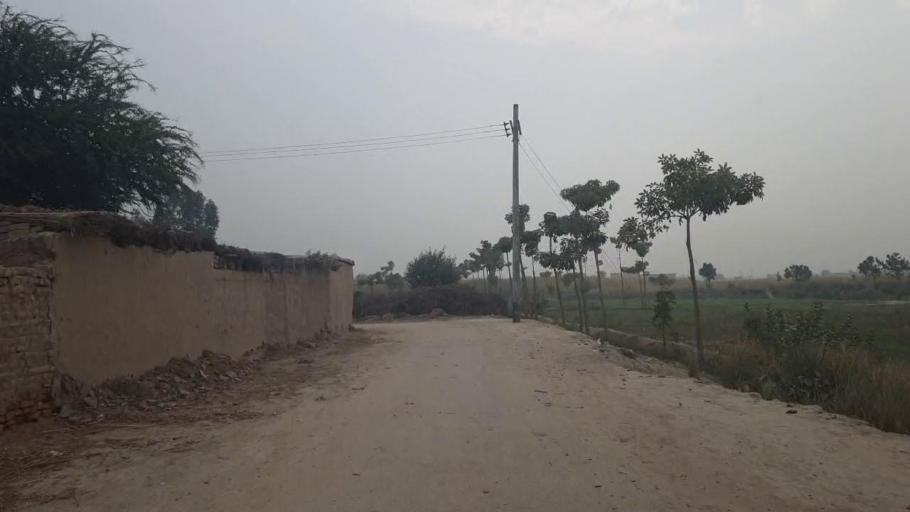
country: PK
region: Sindh
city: Tando Adam
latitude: 25.7459
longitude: 68.6760
